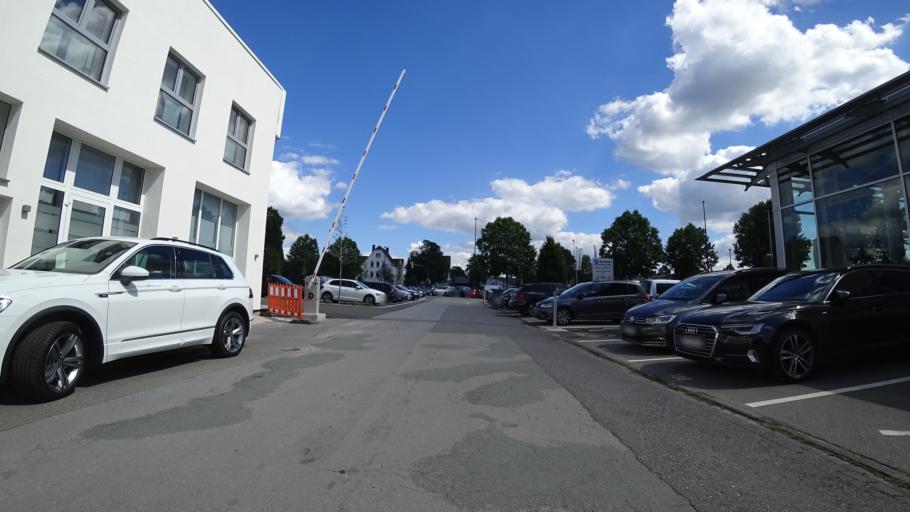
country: DE
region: North Rhine-Westphalia
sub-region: Regierungsbezirk Detmold
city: Guetersloh
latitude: 51.9164
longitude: 8.3905
